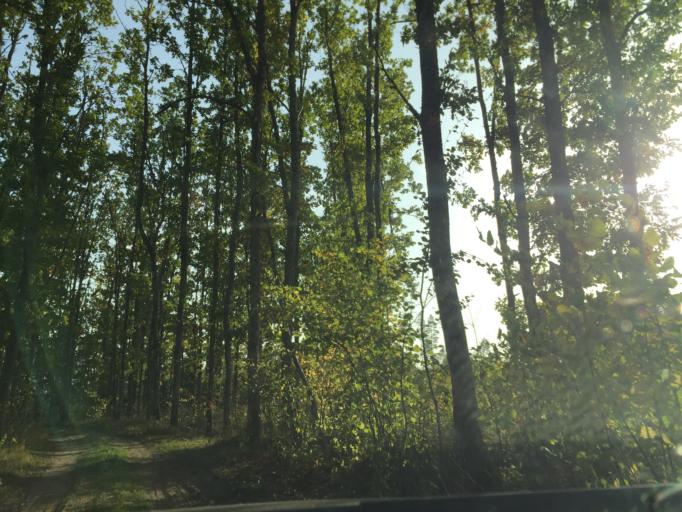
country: LV
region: Garkalne
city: Garkalne
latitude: 56.9704
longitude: 24.4178
